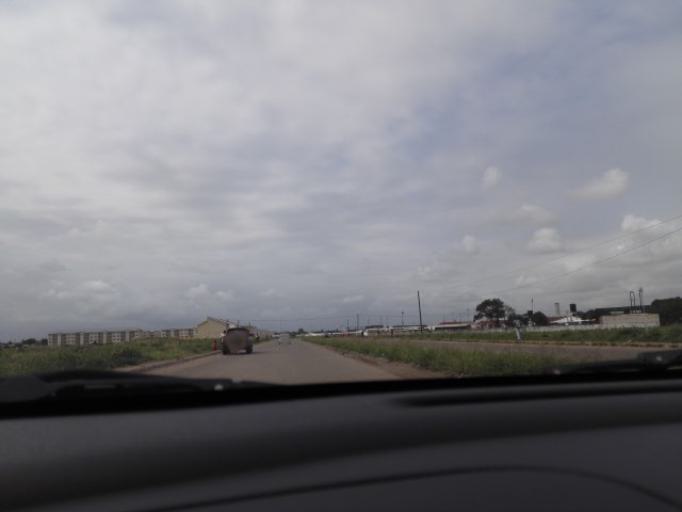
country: MZ
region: Maputo City
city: Maputo
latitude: -25.8212
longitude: 32.5831
